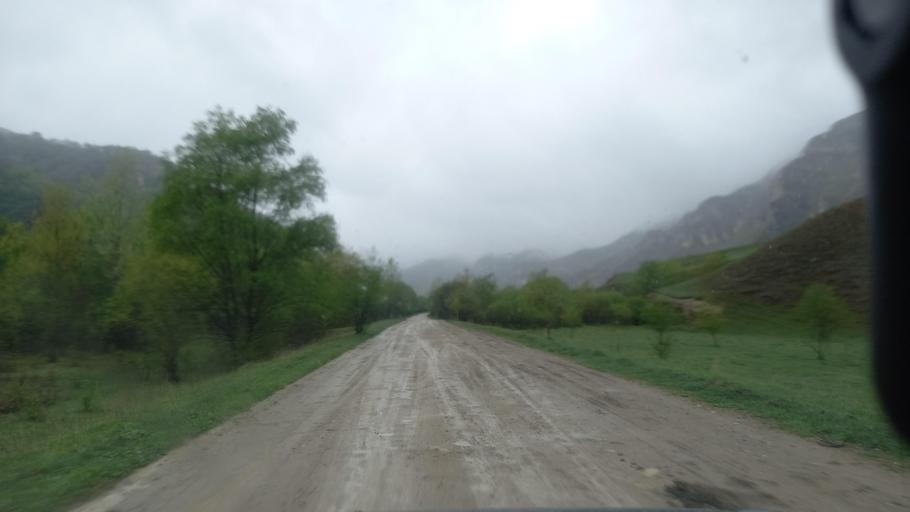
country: RU
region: Kabardino-Balkariya
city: Gundelen
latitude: 43.5984
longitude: 43.0562
